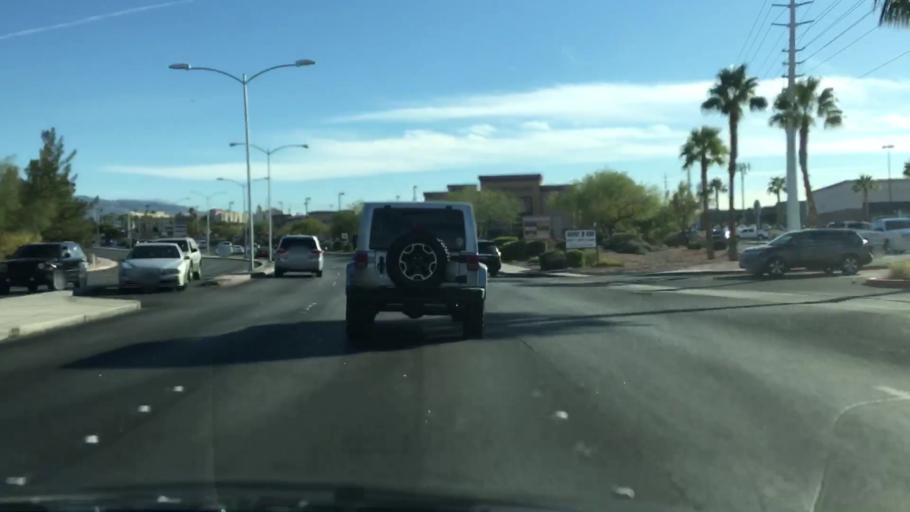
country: US
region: Nevada
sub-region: Clark County
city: Whitney
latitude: 36.0117
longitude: -115.1188
